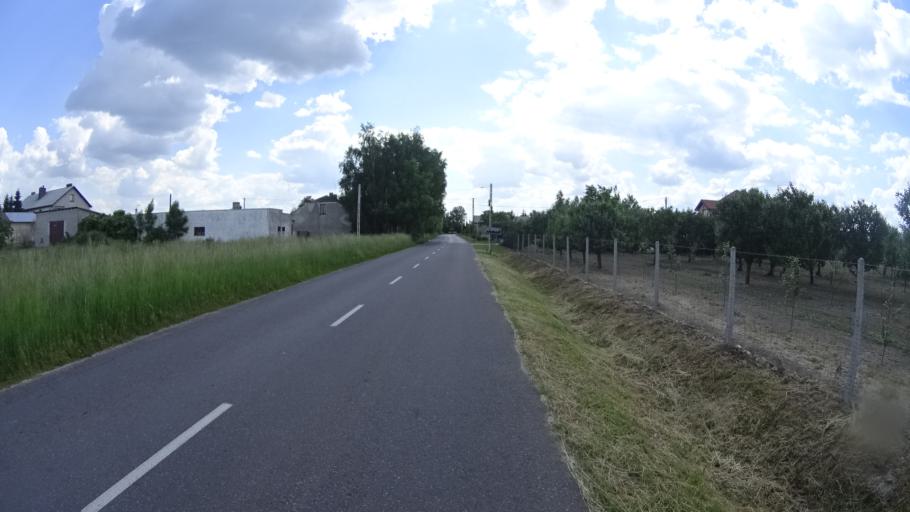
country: PL
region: Masovian Voivodeship
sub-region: Powiat piaseczynski
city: Tarczyn
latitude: 52.0093
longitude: 20.8131
